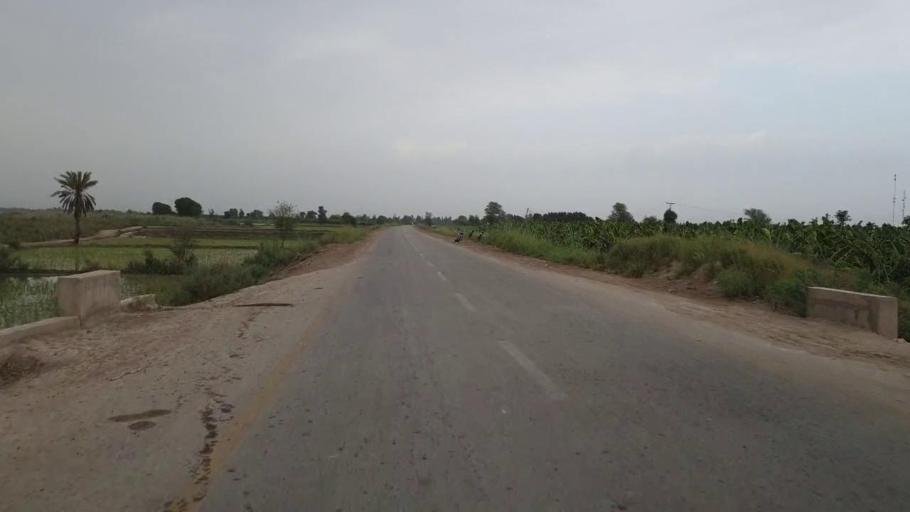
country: PK
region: Sindh
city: Bandhi
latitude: 26.5841
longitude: 68.2834
